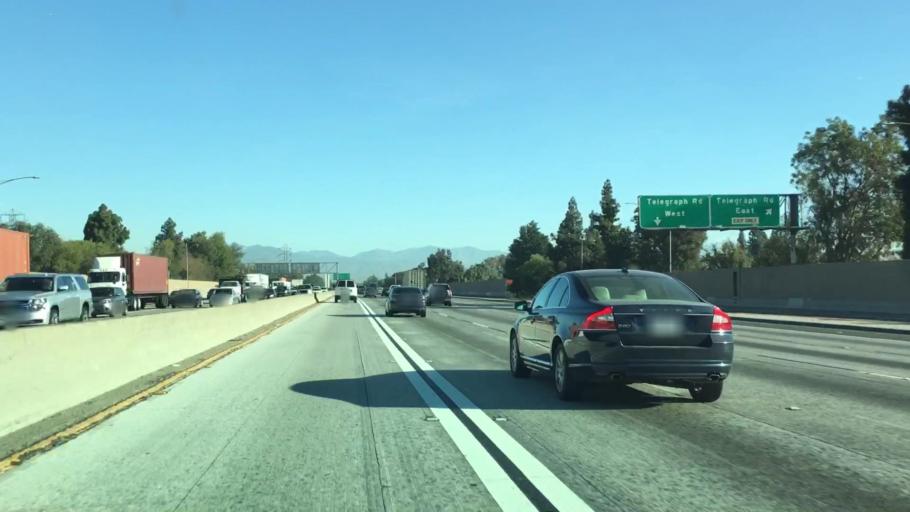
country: US
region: California
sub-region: Los Angeles County
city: Santa Fe Springs
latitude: 33.9469
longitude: -118.0936
